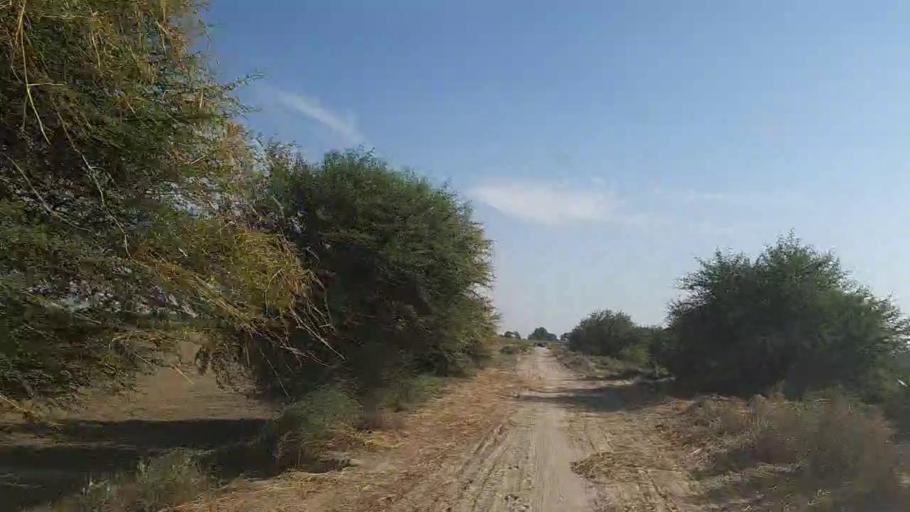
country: PK
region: Sindh
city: Bulri
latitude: 24.8616
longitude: 68.2862
